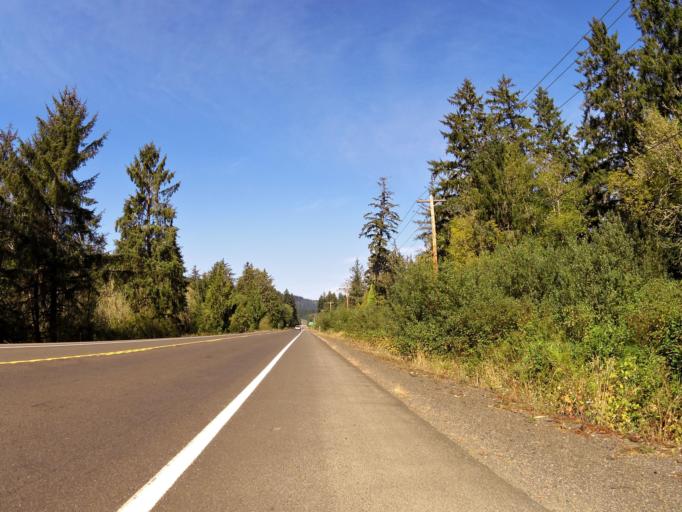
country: US
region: Washington
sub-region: Wahkiakum County
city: Cathlamet
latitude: 46.1422
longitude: -123.3943
